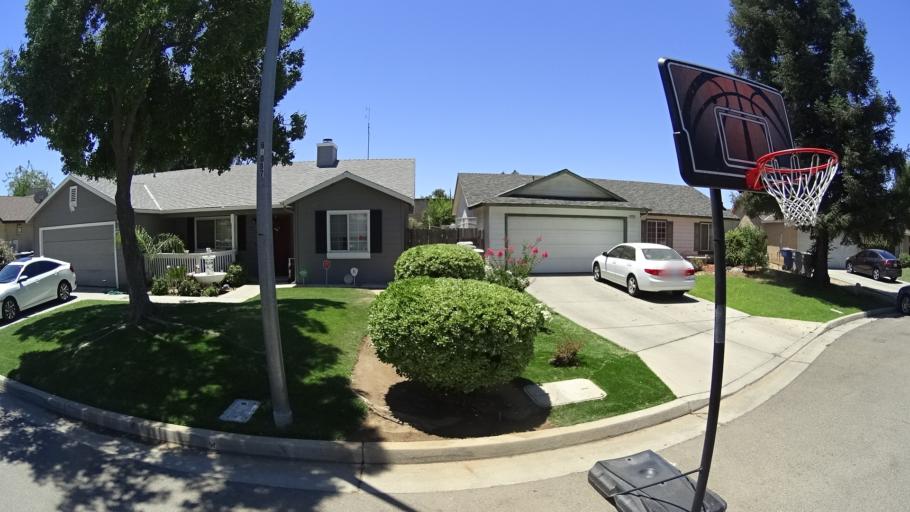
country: US
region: California
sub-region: Fresno County
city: Fresno
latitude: 36.7918
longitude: -119.8146
